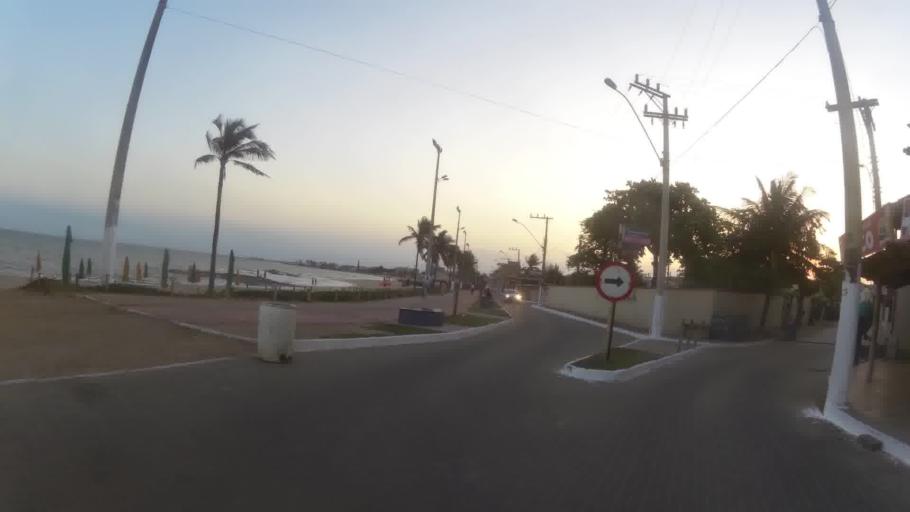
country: BR
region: Espirito Santo
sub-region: Piuma
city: Piuma
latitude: -20.9044
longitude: -40.7776
